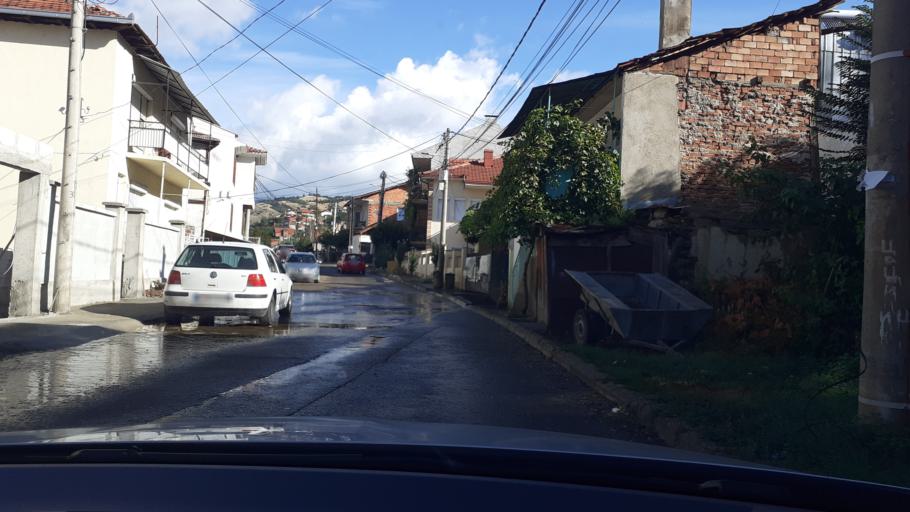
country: MK
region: Kocani
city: Kochani
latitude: 41.9226
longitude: 22.4115
